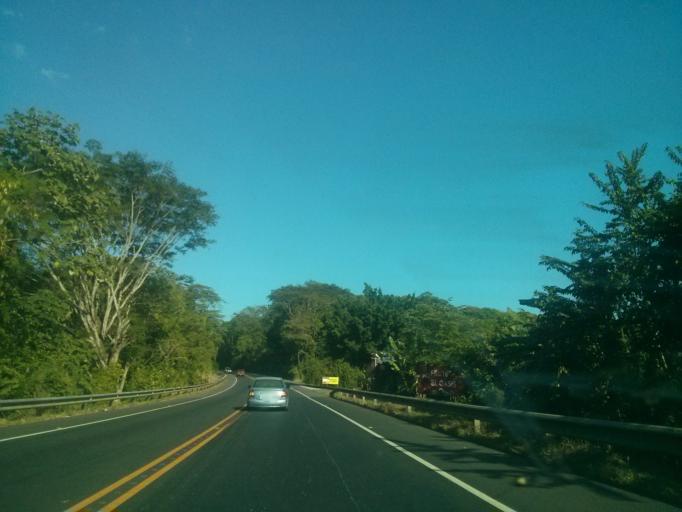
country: CR
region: Alajuela
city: Orotina
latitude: 9.8996
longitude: -84.5362
